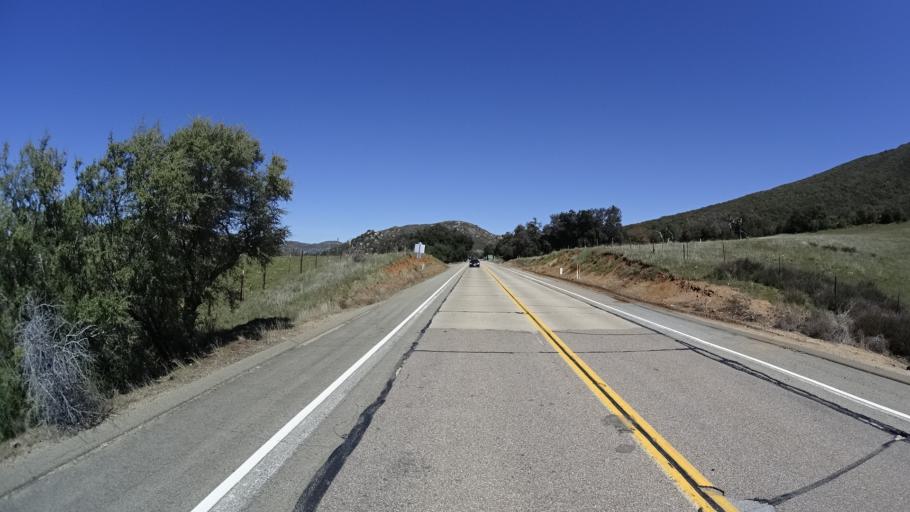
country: US
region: California
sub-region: San Diego County
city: Descanso
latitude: 32.8493
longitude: -116.5977
